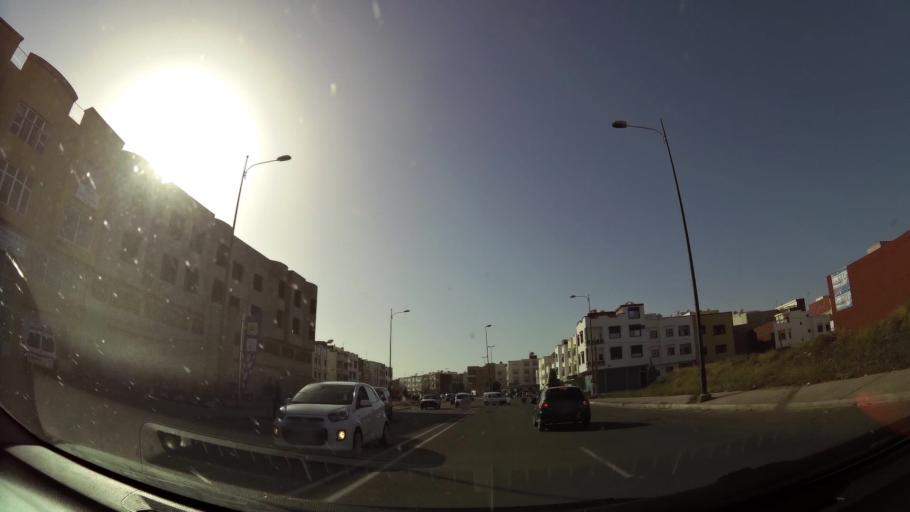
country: MA
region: Oued ed Dahab-Lagouira
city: Dakhla
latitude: 30.3935
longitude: -9.5330
